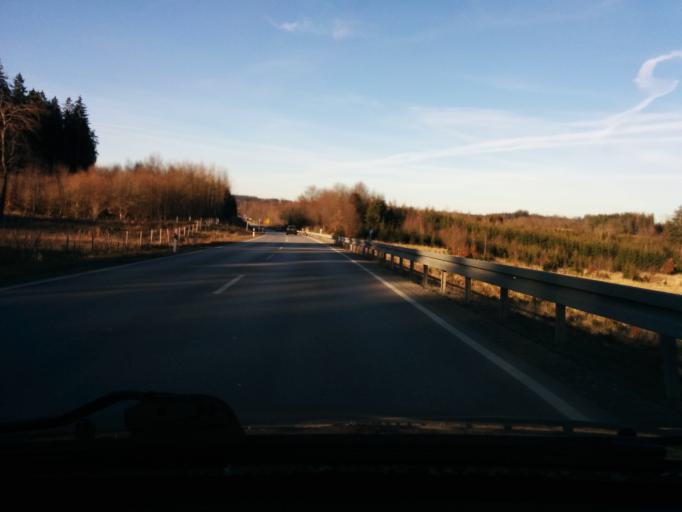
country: DE
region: Bavaria
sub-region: Upper Bavaria
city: Gilching
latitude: 48.0871
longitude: 11.3183
